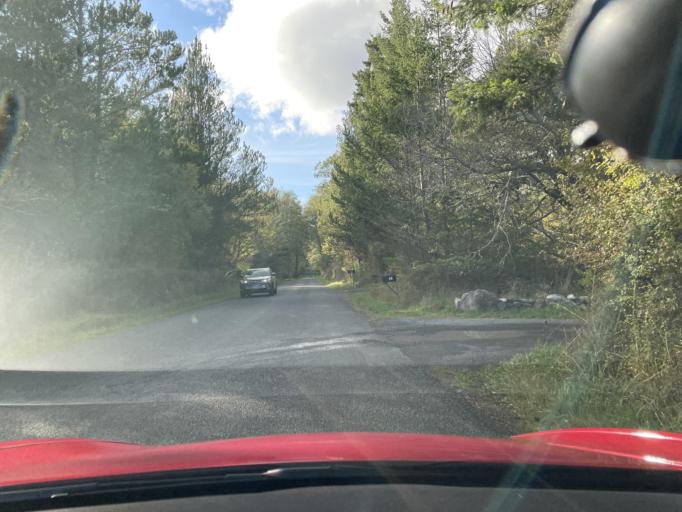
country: US
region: Washington
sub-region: San Juan County
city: Friday Harbor
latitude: 48.4818
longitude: -123.0336
